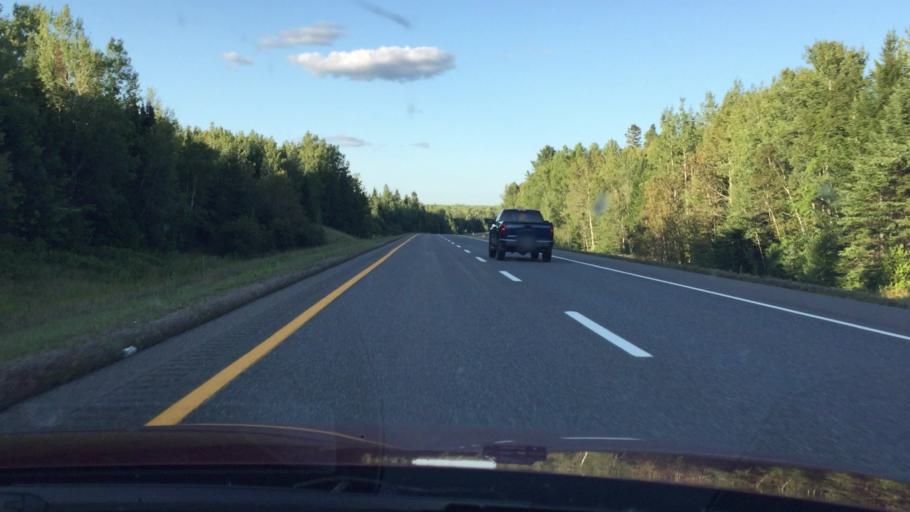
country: US
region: Maine
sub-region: Penobscot County
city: Patten
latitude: 46.0394
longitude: -68.2646
